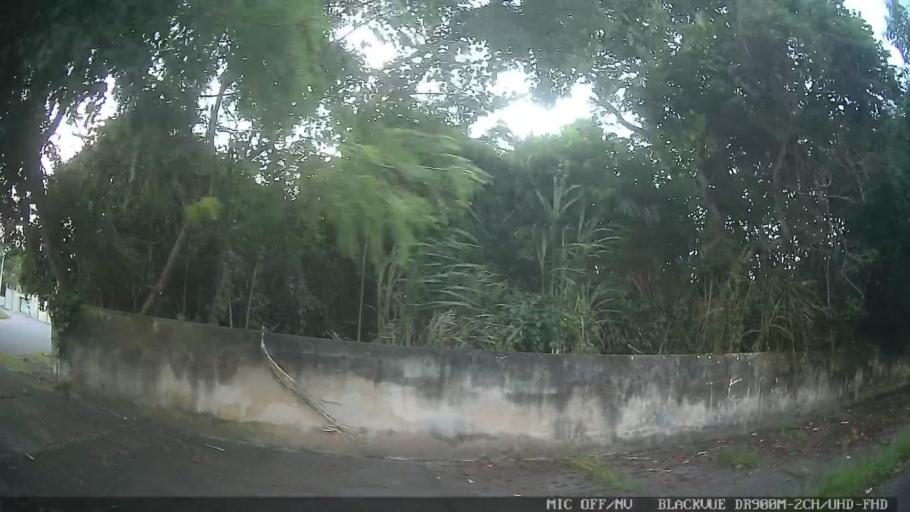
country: BR
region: Sao Paulo
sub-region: Caraguatatuba
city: Caraguatatuba
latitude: -23.6862
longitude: -45.4357
